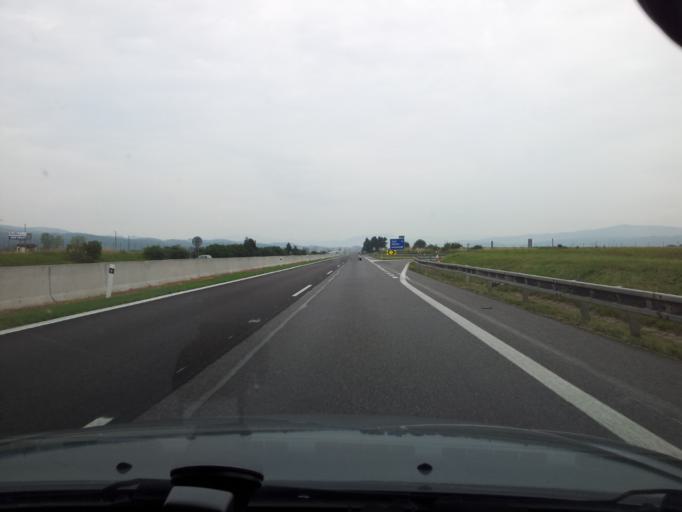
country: SK
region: Banskobystricky
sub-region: Okres Banska Bystrica
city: Zvolen
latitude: 48.6290
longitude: 19.1192
